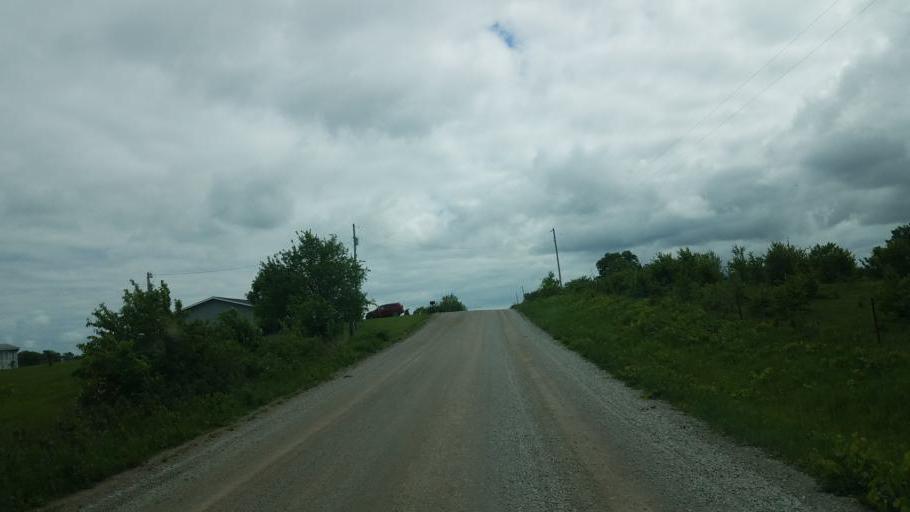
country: US
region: Iowa
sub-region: Decatur County
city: Lamoni
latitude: 40.6047
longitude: -93.8440
